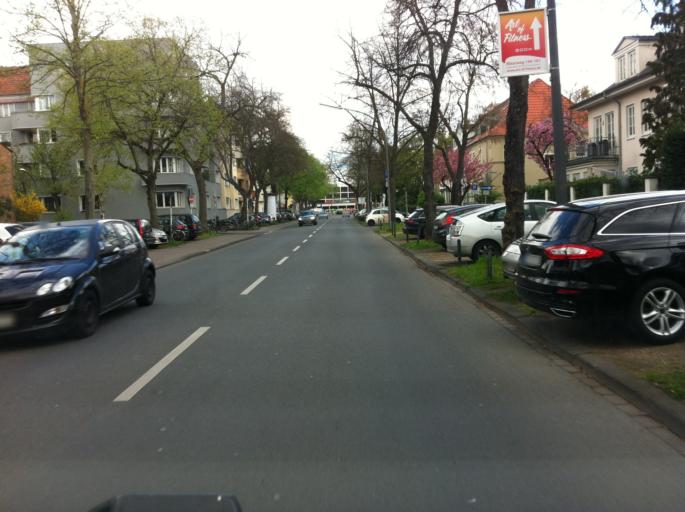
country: DE
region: North Rhine-Westphalia
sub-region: Regierungsbezirk Koln
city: Neuehrenfeld
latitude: 50.9348
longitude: 6.9008
